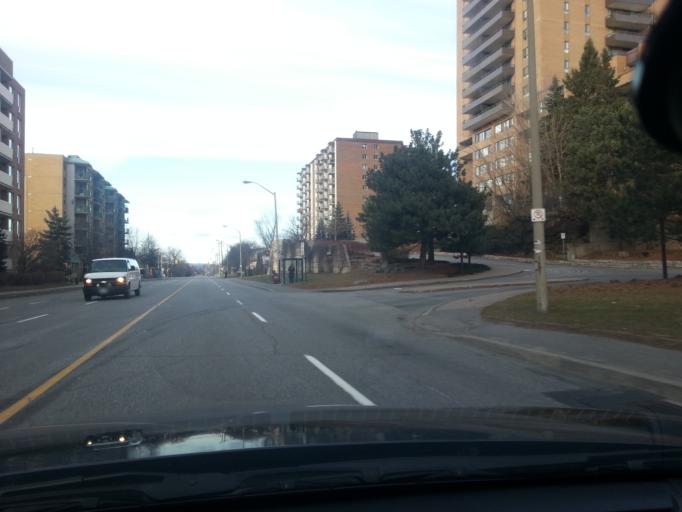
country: CA
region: Ontario
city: Ottawa
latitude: 45.4439
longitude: -75.6484
